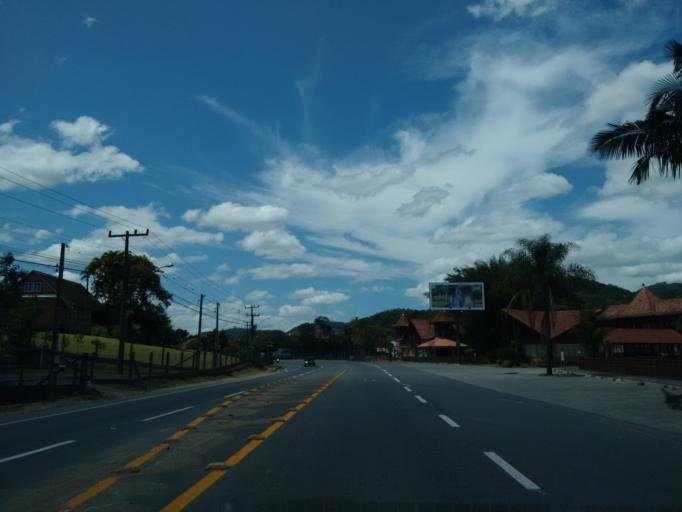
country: BR
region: Santa Catarina
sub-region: Pomerode
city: Pomerode
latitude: -26.7656
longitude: -49.1697
